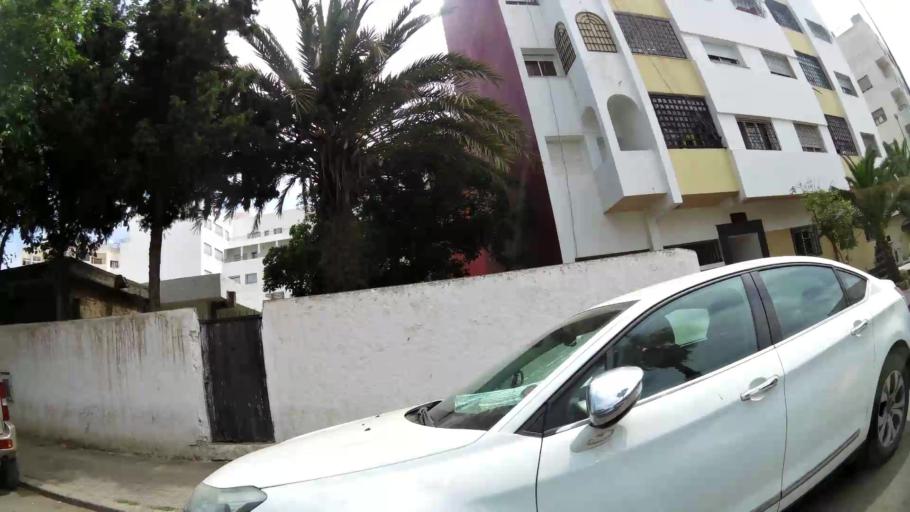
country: MA
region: Rabat-Sale-Zemmour-Zaer
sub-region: Rabat
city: Rabat
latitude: 34.0153
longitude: -6.8493
